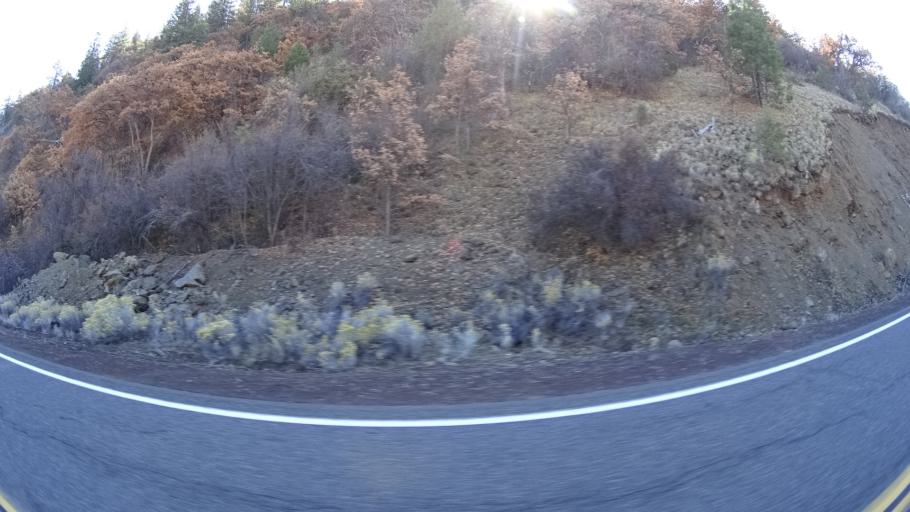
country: US
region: California
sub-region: Siskiyou County
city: Weed
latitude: 41.4718
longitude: -122.5878
